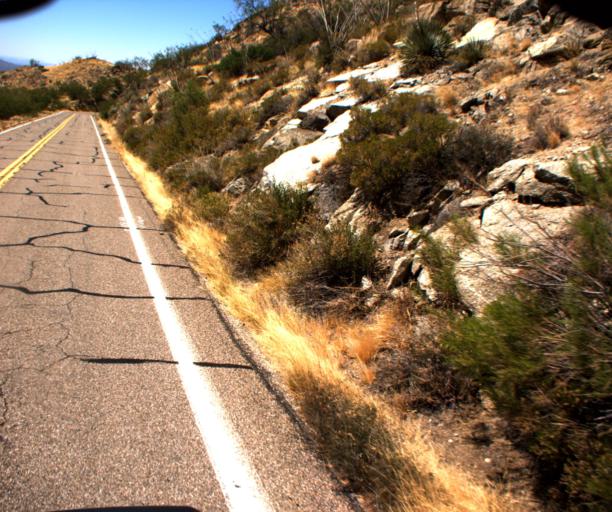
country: US
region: Arizona
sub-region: Pima County
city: Sells
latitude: 31.9834
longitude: -111.6008
